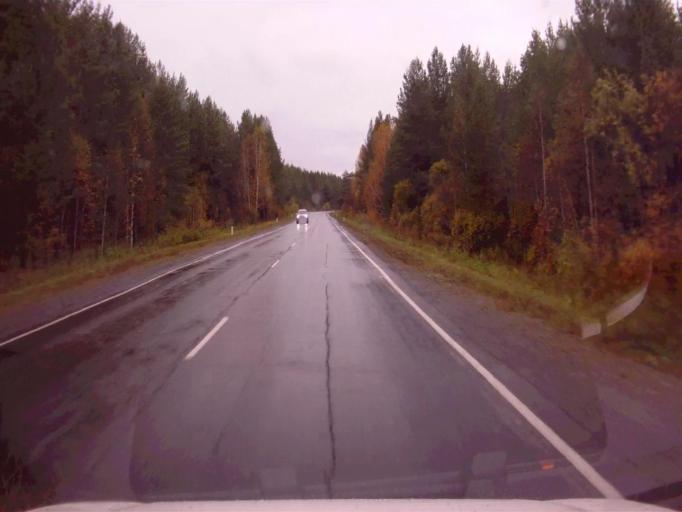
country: RU
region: Chelyabinsk
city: Verkhniy Ufaley
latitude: 56.0119
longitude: 60.3176
